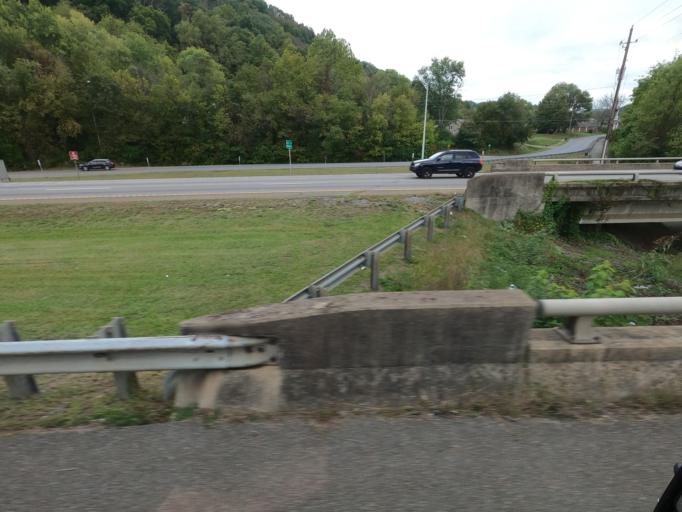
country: US
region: Tennessee
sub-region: Carter County
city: Elizabethton
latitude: 36.3438
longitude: -82.2072
